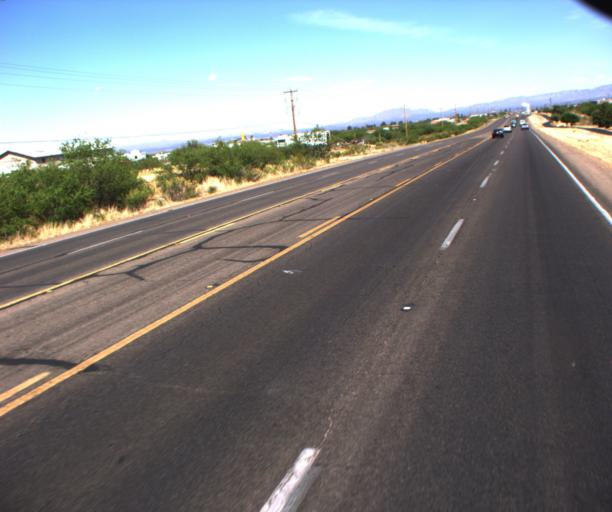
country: US
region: Arizona
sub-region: Cochise County
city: Sierra Vista
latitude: 31.5546
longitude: -110.2382
